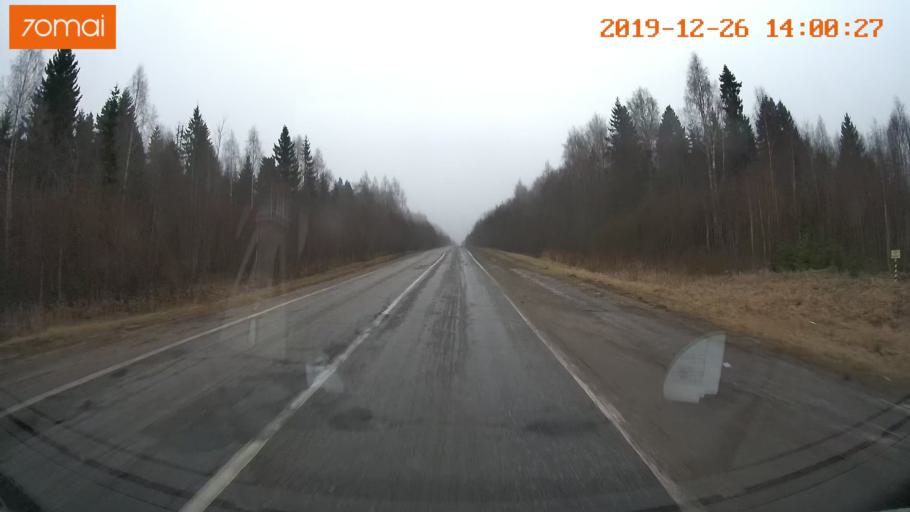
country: RU
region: Jaroslavl
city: Poshekhon'ye
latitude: 58.5581
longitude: 38.7436
